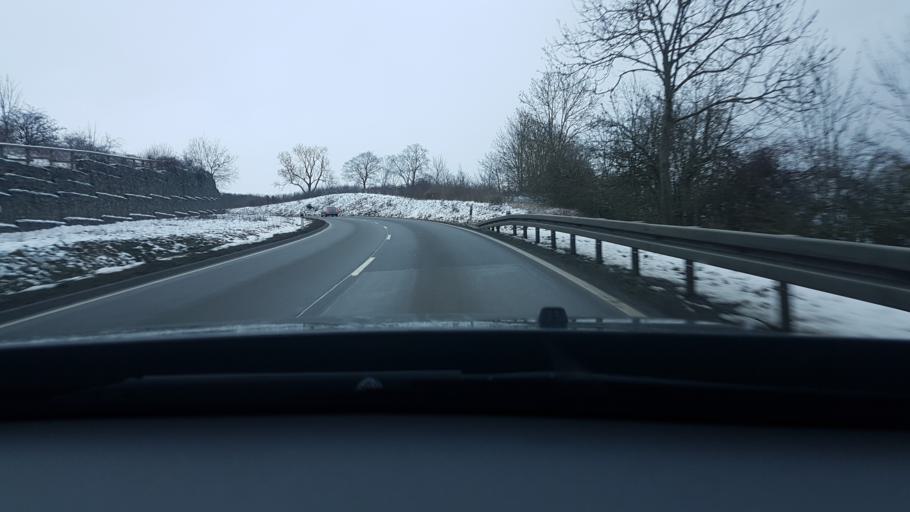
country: DE
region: Hesse
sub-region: Regierungsbezirk Kassel
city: Korbach
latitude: 51.3108
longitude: 8.8561
